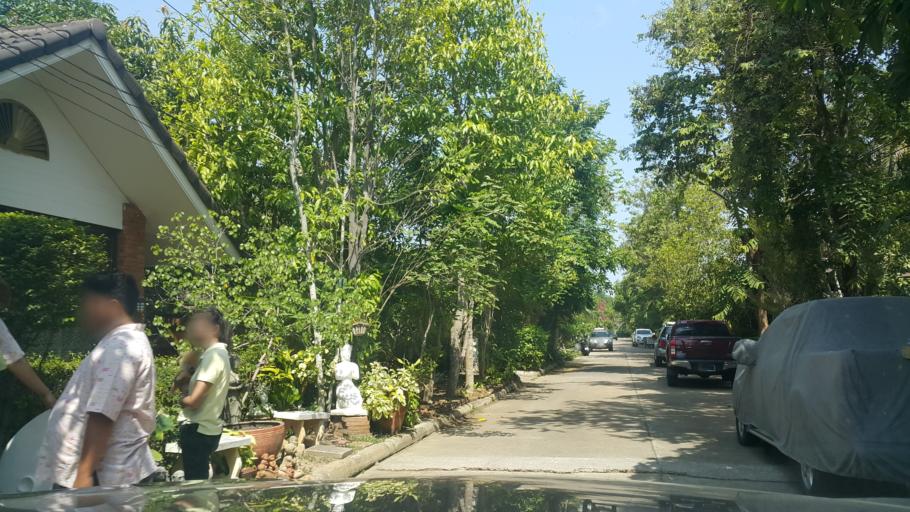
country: TH
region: Chiang Mai
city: Chiang Mai
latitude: 18.7290
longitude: 98.9710
